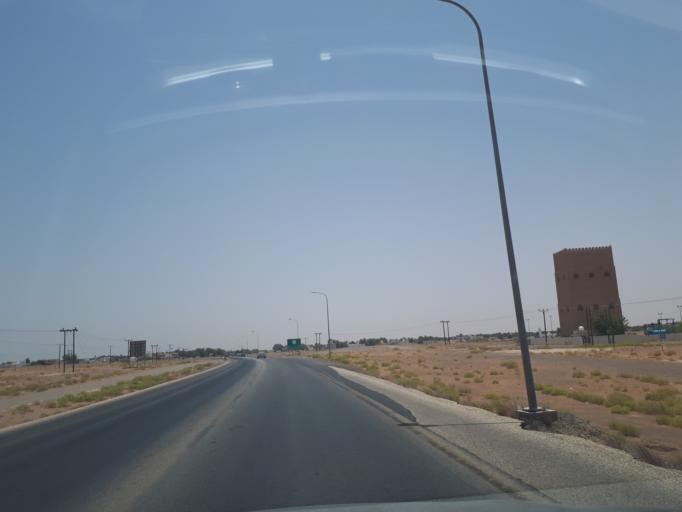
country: OM
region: Ash Sharqiyah
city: Al Qabil
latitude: 22.5098
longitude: 58.7409
